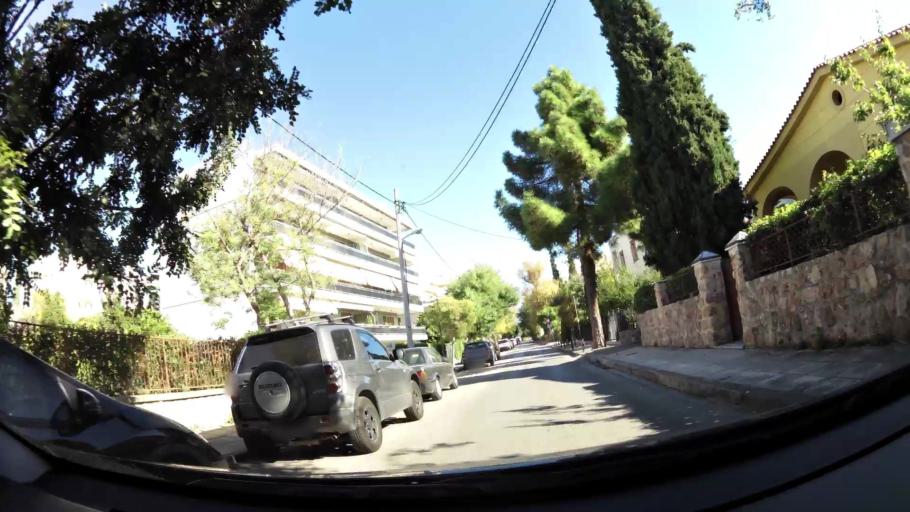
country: GR
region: Attica
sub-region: Nomarchia Athinas
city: Khalandrion
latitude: 38.0248
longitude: 23.8107
